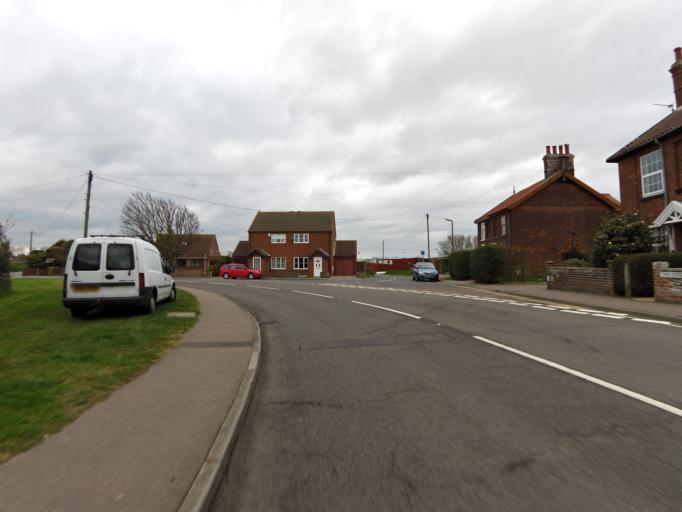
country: GB
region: England
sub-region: Norfolk
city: Hopton on Sea
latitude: 52.5177
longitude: 1.7466
